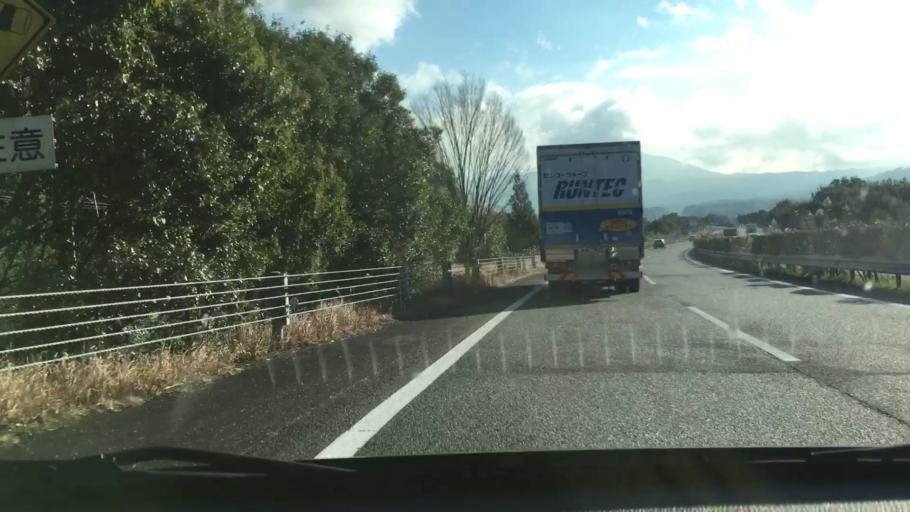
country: JP
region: Kumamoto
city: Hitoyoshi
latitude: 32.0615
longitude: 130.8038
